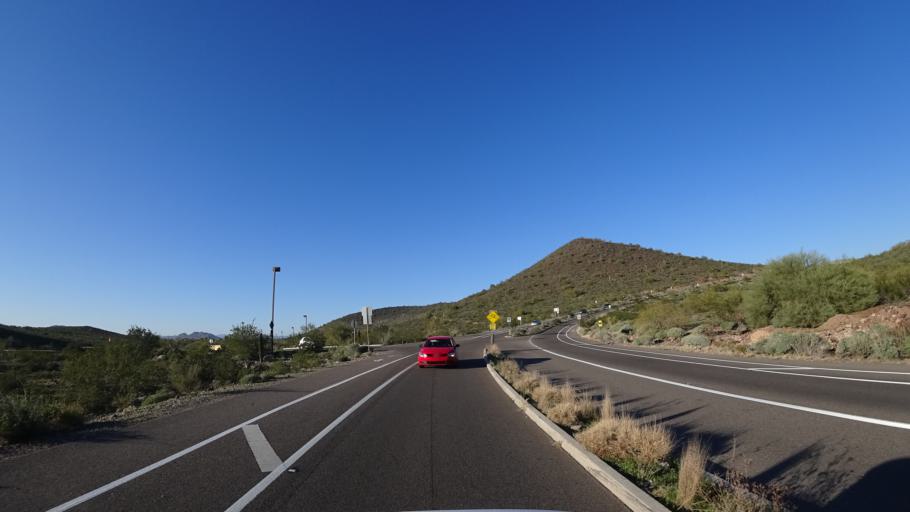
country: US
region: Arizona
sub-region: Maricopa County
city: Peoria
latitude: 33.6897
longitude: -112.1881
